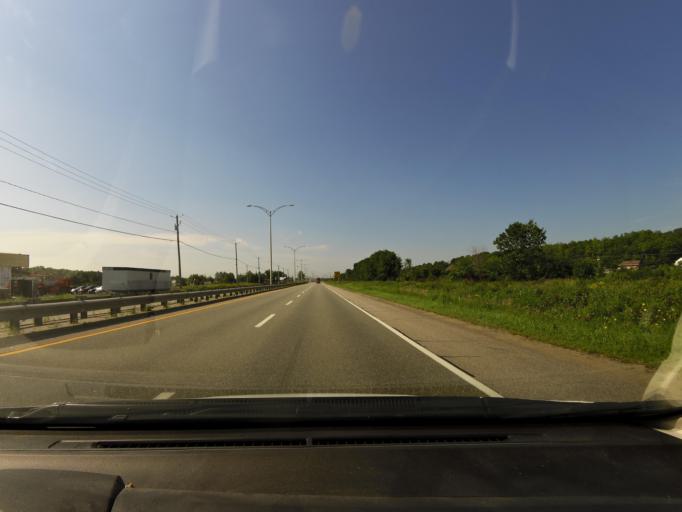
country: CA
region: Quebec
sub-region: Capitale-Nationale
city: Chateau-Richer
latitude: 46.9396
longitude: -71.0547
